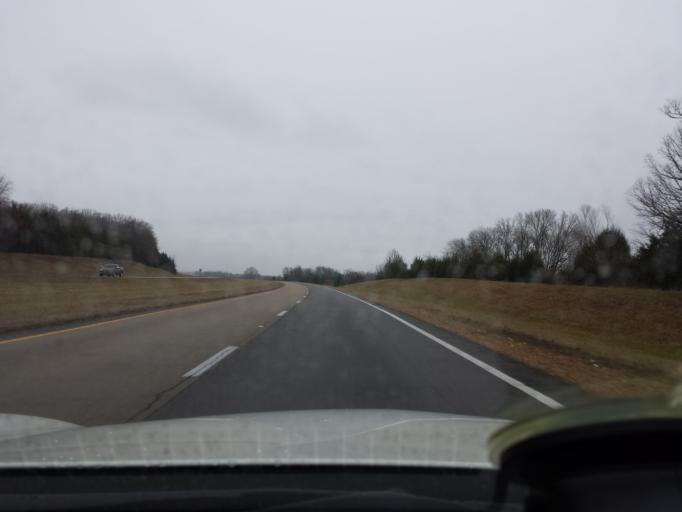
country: US
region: Mississippi
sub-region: Chickasaw County
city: Okolona
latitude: 33.9875
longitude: -88.7019
